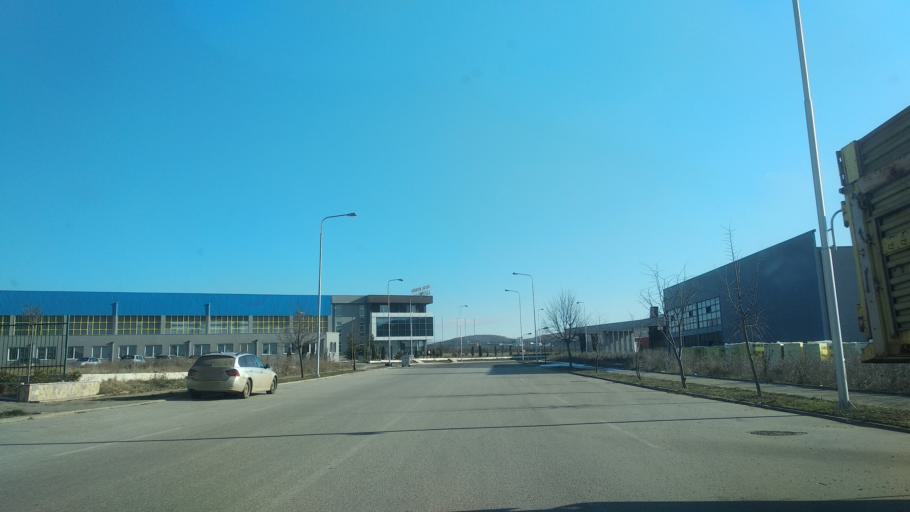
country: XK
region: Pristina
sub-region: Komuna e Drenasit
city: Glogovac
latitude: 42.6007
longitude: 20.9647
